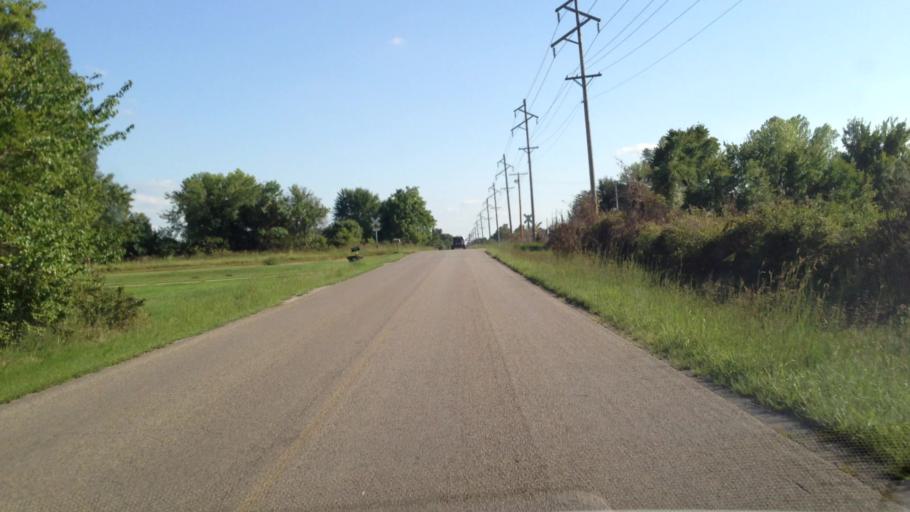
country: US
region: Kansas
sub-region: Crawford County
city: Frontenac
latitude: 37.4643
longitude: -94.6308
